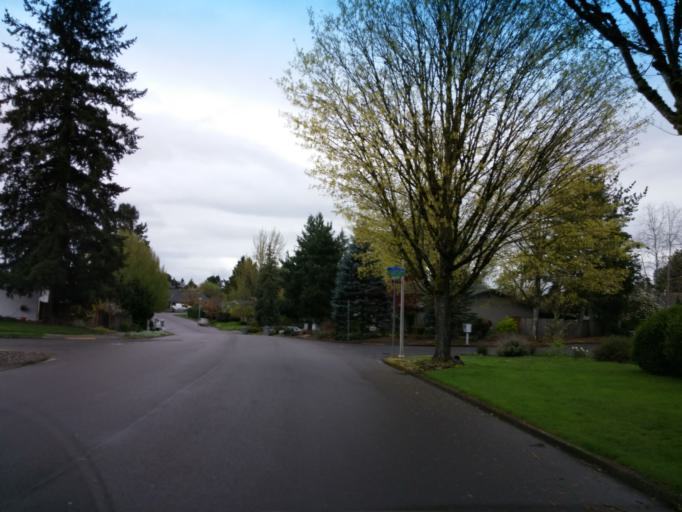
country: US
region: Oregon
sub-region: Washington County
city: Oak Hills
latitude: 45.5375
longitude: -122.8396
